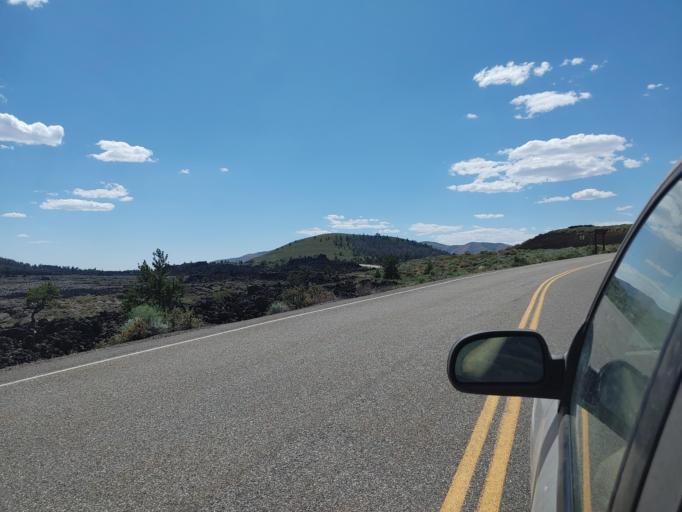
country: US
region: Idaho
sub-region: Butte County
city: Arco
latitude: 43.4616
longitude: -113.5622
